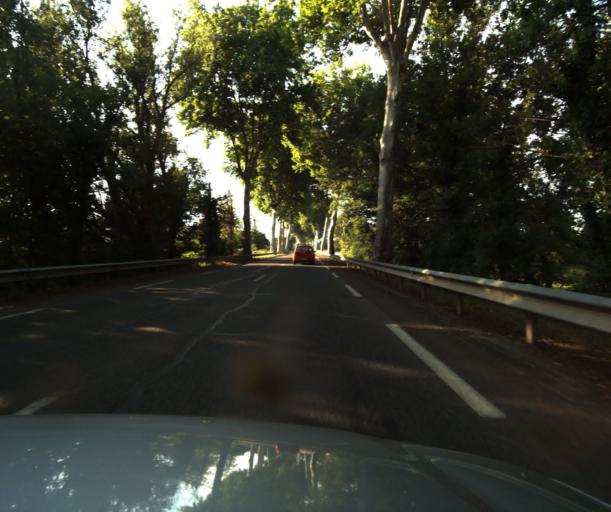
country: FR
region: Midi-Pyrenees
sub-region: Departement du Tarn-et-Garonne
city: Moissac
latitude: 44.0803
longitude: 1.0912
